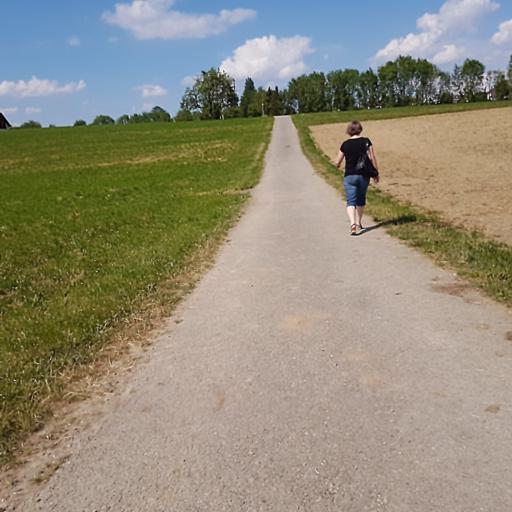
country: CH
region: Thurgau
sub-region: Arbon District
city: Amriswil
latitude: 47.5550
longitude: 9.3019
